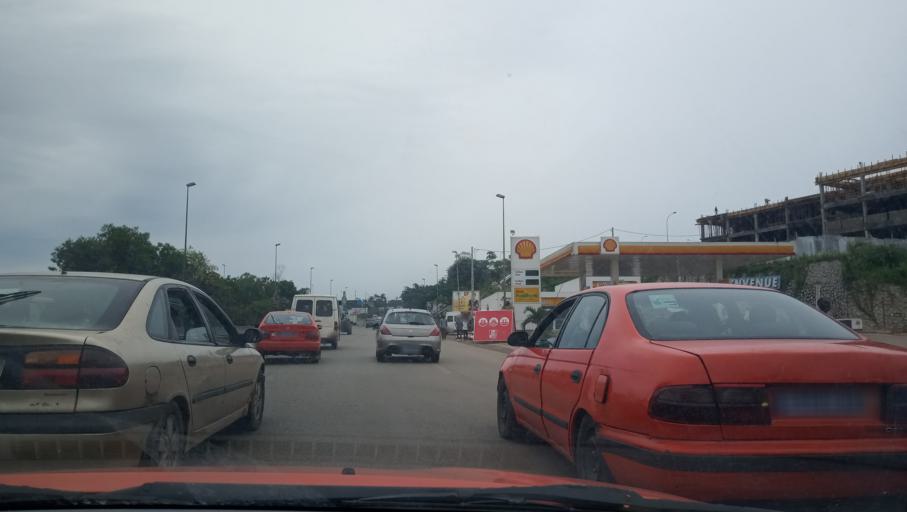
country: CI
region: Lagunes
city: Abidjan
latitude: 5.3545
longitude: -4.0107
